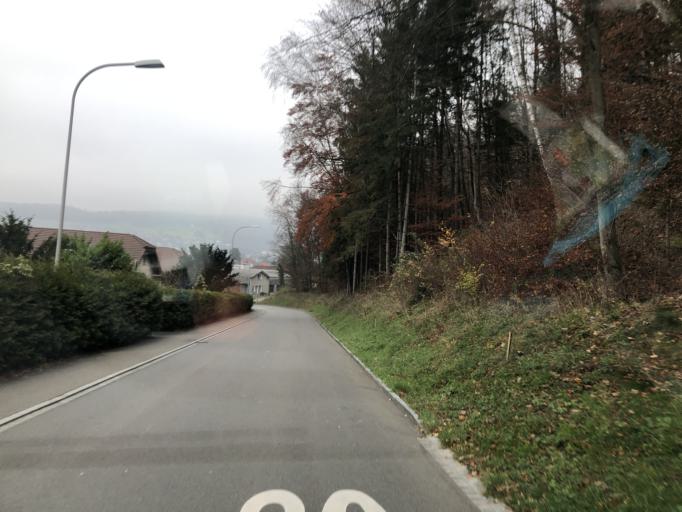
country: CH
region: Aargau
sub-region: Bezirk Baden
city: Gebenstorf
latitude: 47.4877
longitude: 8.2450
